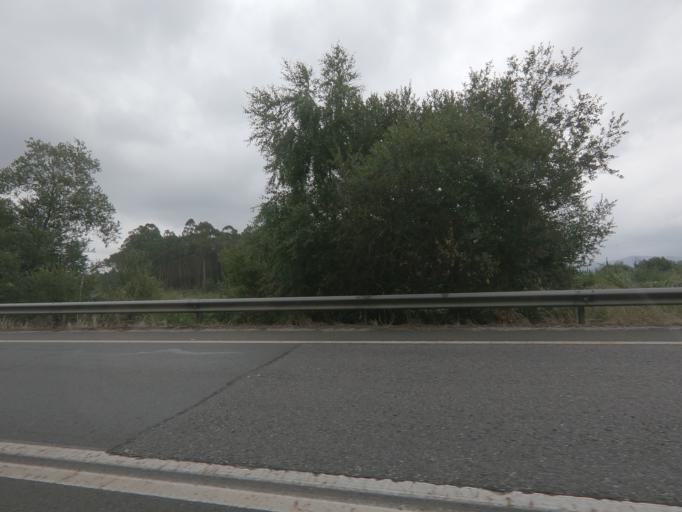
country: ES
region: Galicia
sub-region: Provincia de Pontevedra
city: Tomino
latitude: 41.9857
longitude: -8.7172
